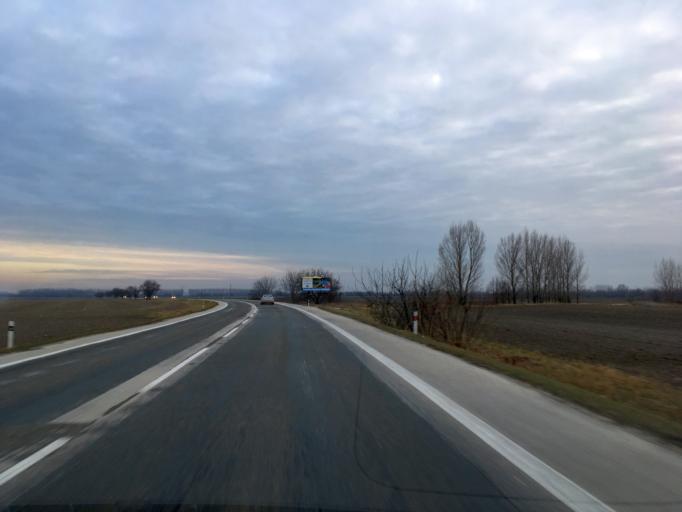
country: SK
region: Trnavsky
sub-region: Okres Dunajska Streda
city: Velky Meder
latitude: 47.9277
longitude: 17.7227
